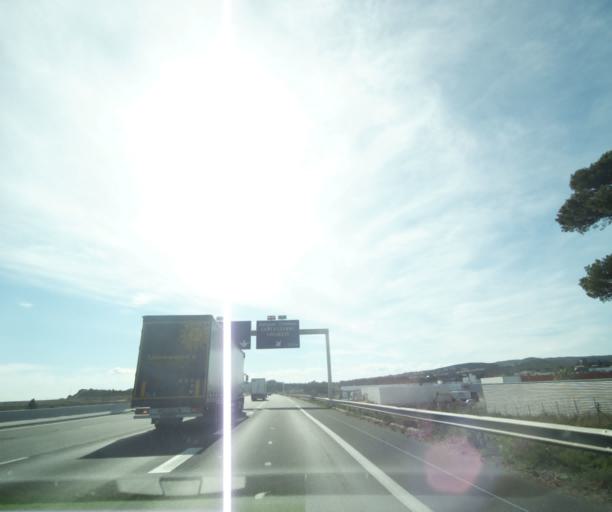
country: FR
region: Languedoc-Roussillon
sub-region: Departement de l'Aude
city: Narbonne
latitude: 43.1559
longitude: 2.9865
